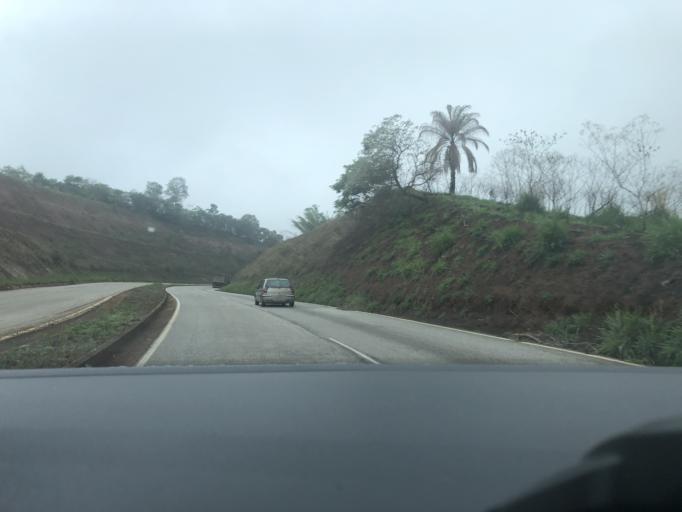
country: BR
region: Minas Gerais
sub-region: Congonhas
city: Congonhas
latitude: -20.5914
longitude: -43.9476
